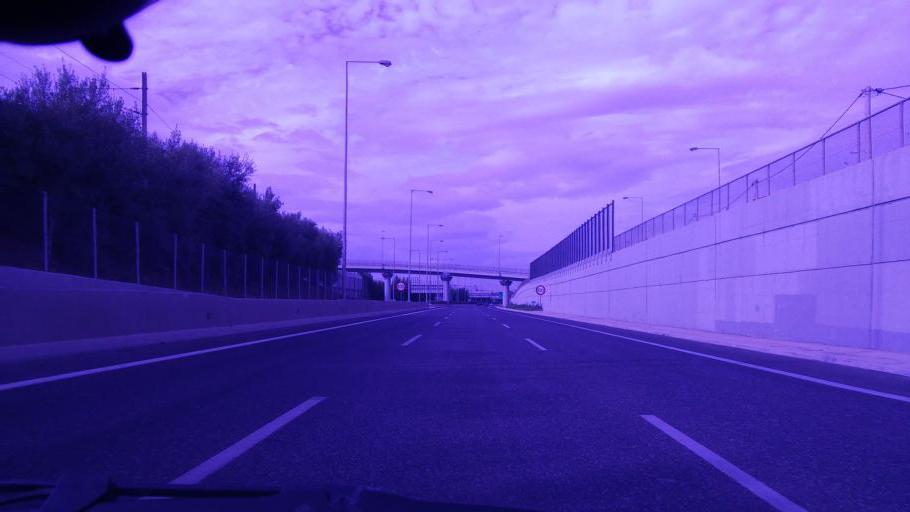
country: GR
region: Attica
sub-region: Nomarchia Dytikis Attikis
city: Ano Liosia
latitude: 38.0722
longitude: 23.7007
